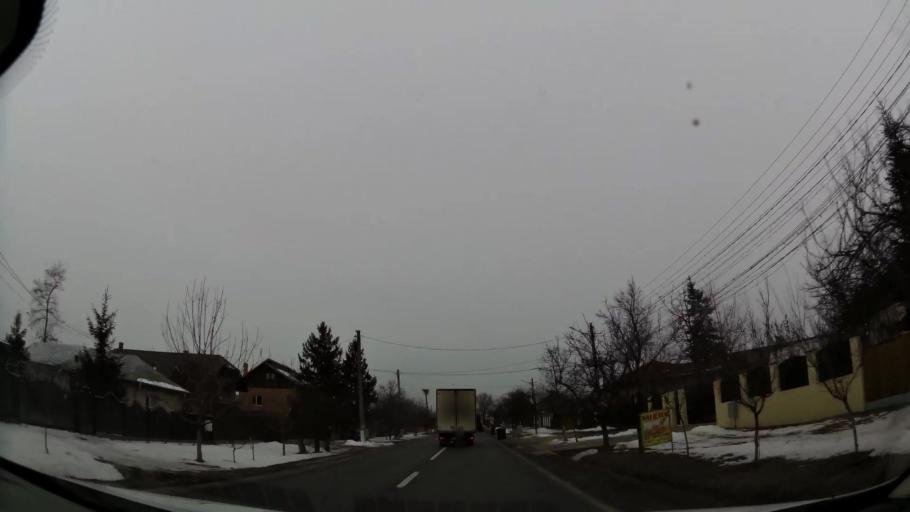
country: RO
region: Dambovita
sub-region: Comuna Tartasesti
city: Baldana
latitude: 44.6008
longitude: 25.7812
